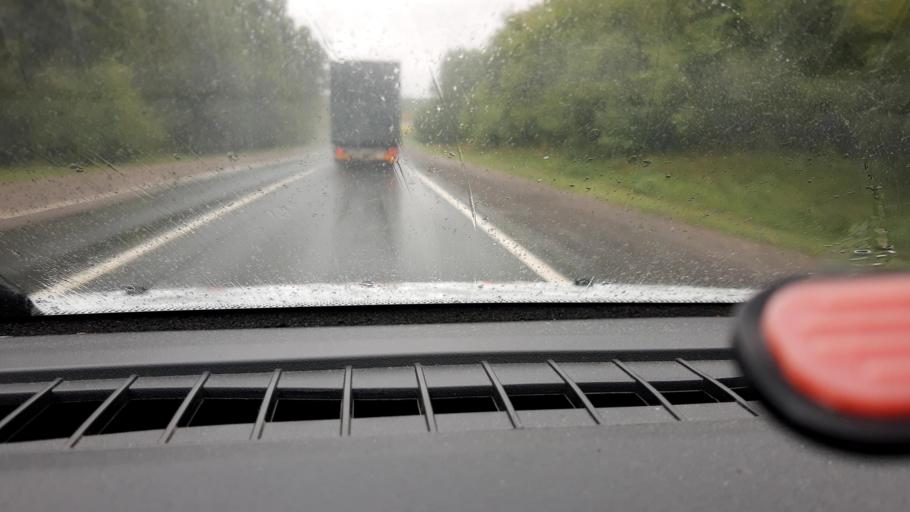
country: RU
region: Nizjnij Novgorod
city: Lyskovo
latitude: 56.0102
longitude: 44.8580
